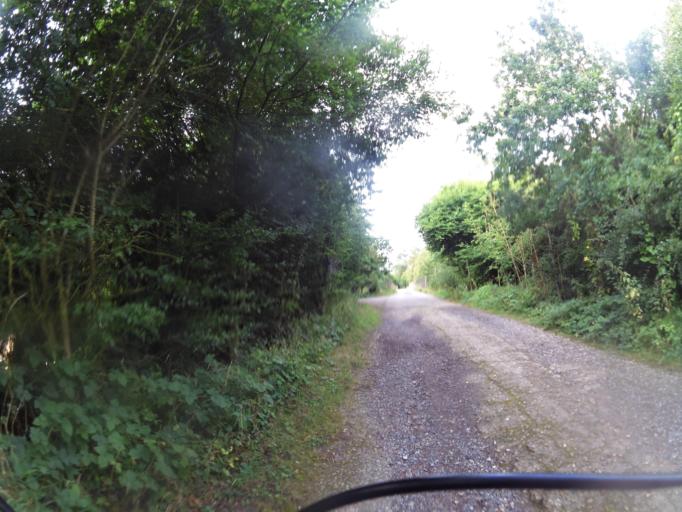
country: GB
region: England
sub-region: Suffolk
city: Ipswich
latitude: 52.0275
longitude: 1.1271
